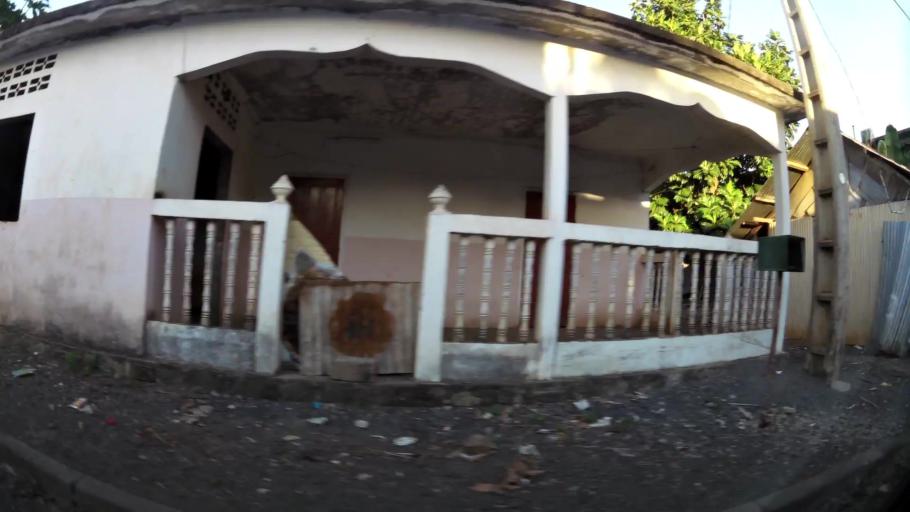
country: YT
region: Dembeni
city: Dembeni
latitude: -12.8441
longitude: 45.1921
